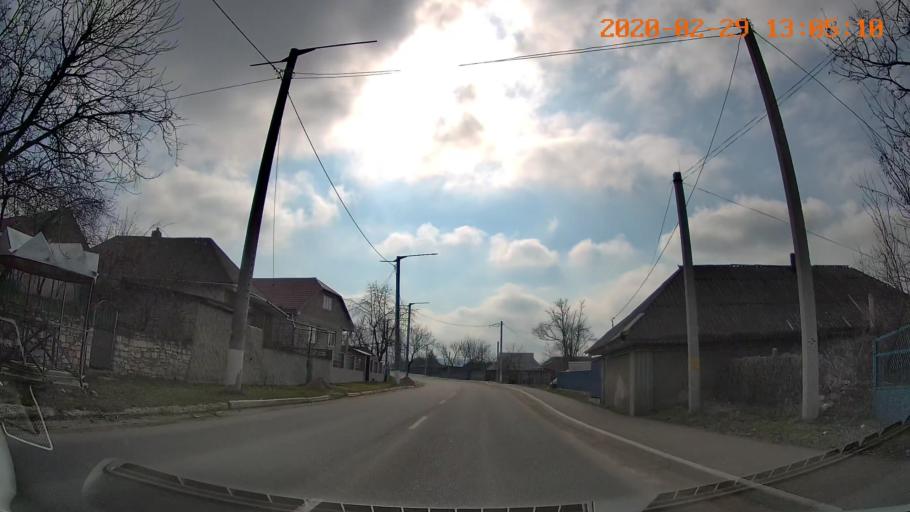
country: MD
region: Telenesti
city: Camenca
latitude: 48.0225
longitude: 28.7081
